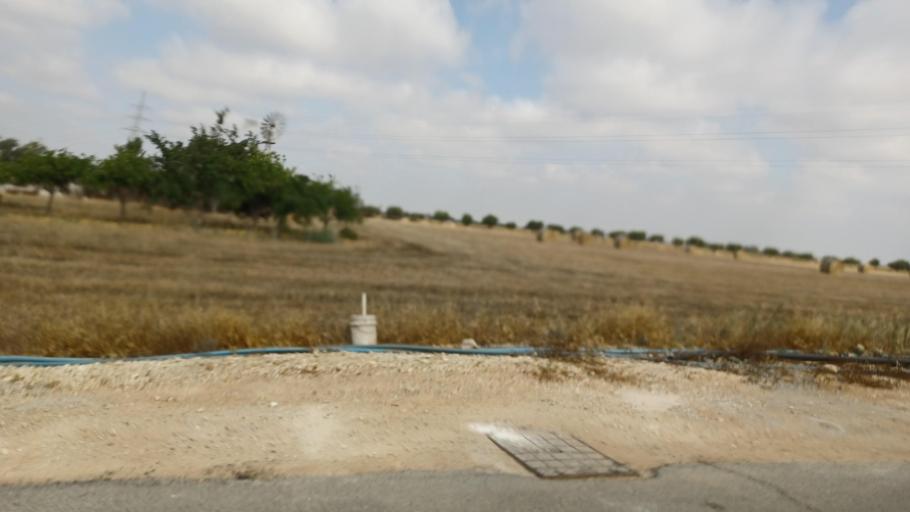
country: CY
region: Ammochostos
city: Ayia Napa
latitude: 35.0057
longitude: 34.0057
